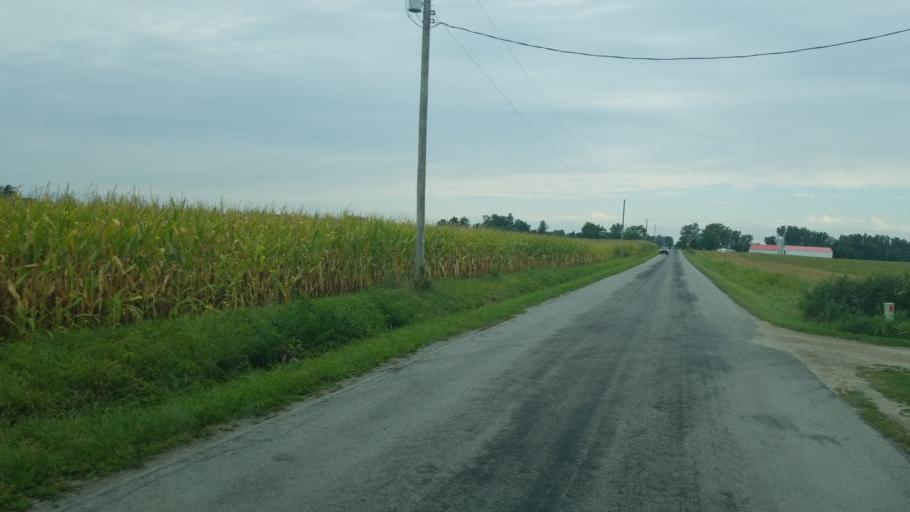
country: US
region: Ohio
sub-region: Wyandot County
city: Upper Sandusky
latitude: 40.8358
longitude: -83.1889
